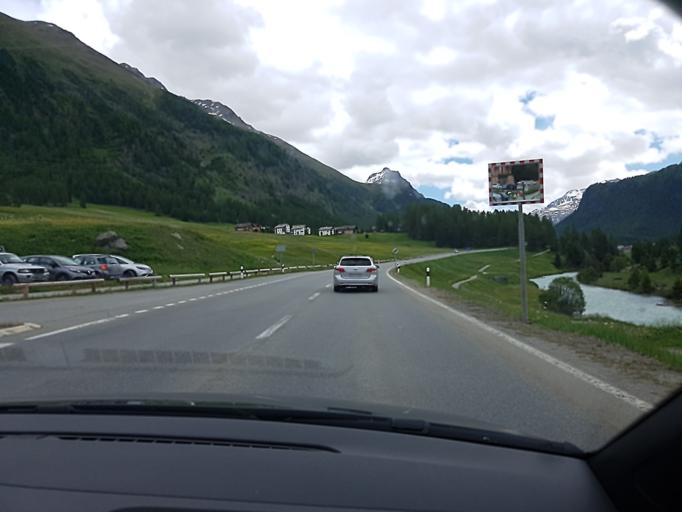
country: CH
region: Grisons
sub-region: Maloja District
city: Pontresina
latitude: 46.5082
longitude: 9.8828
